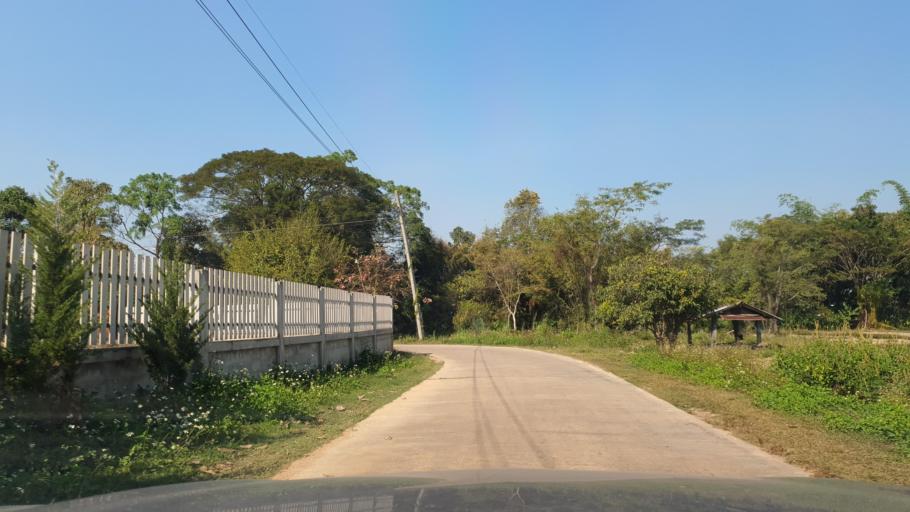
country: TH
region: Chiang Rai
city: Mae Lao
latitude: 19.7982
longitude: 99.7024
